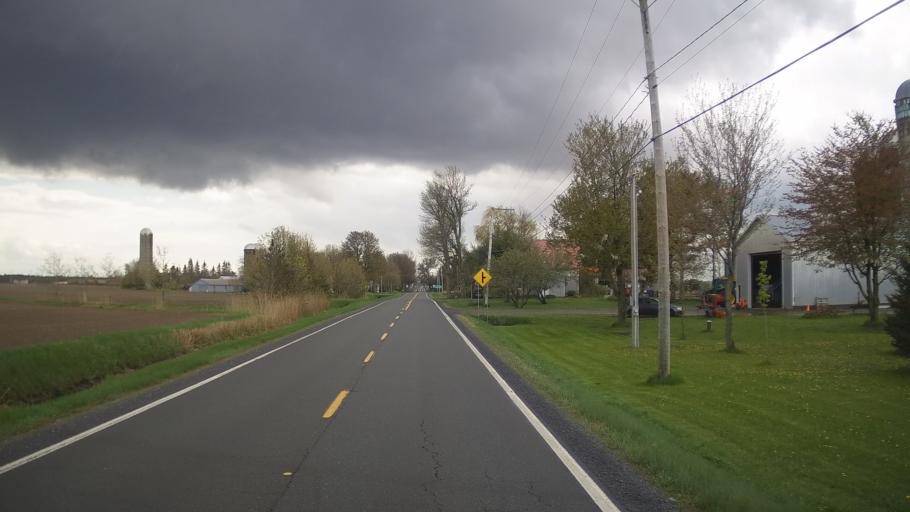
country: CA
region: Quebec
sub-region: Monteregie
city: Farnham
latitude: 45.3055
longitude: -73.1104
